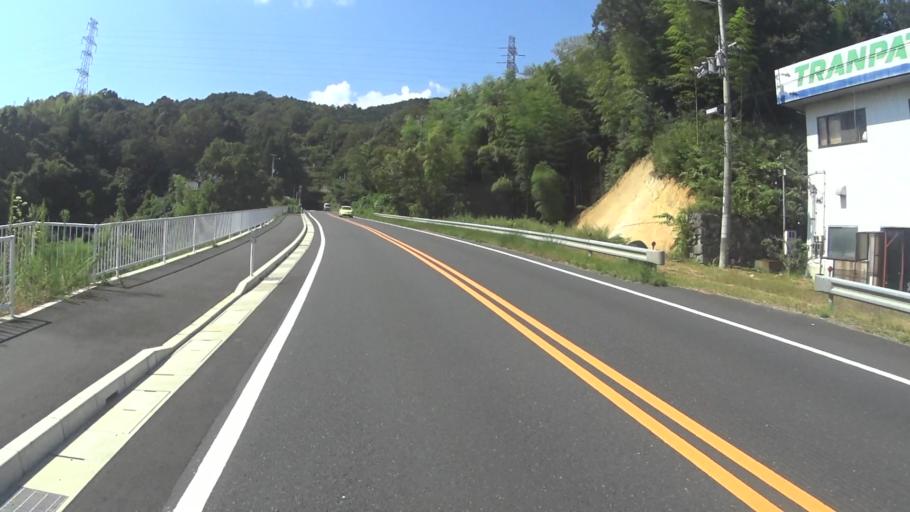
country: JP
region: Kyoto
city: Miyazu
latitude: 35.5518
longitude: 135.2270
